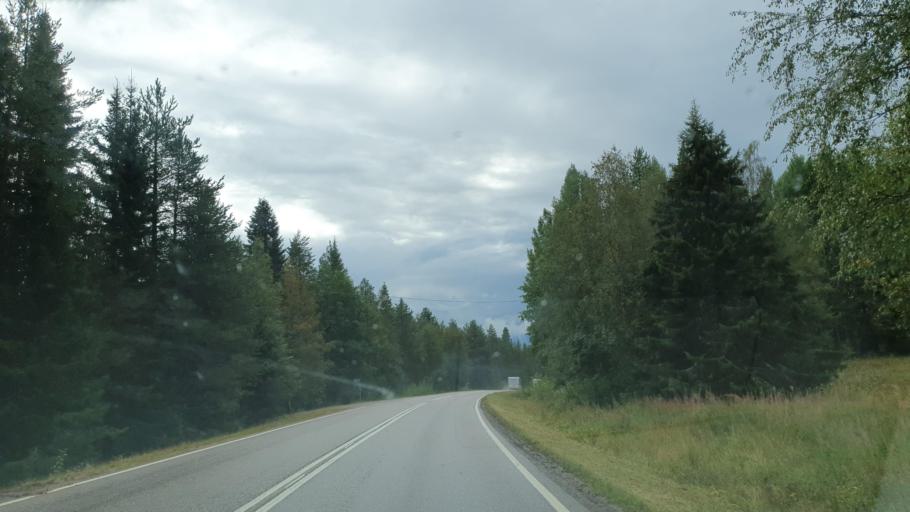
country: FI
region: Kainuu
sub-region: Kehys-Kainuu
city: Puolanka
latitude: 64.9989
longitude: 27.6700
